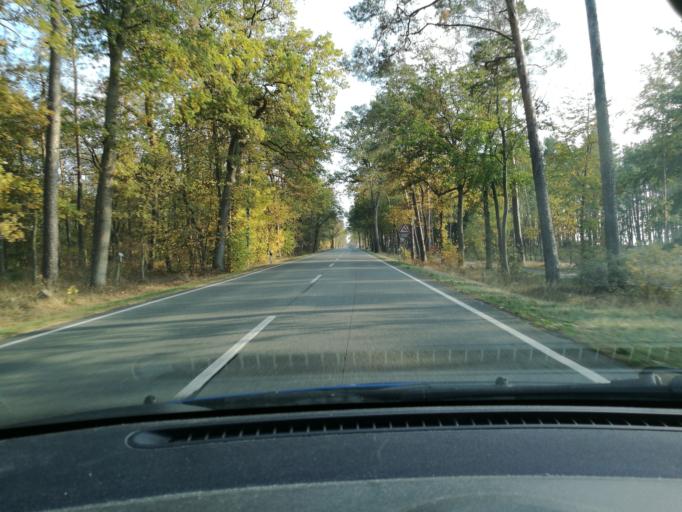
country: DE
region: Lower Saxony
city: Kusten
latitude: 52.9991
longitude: 11.1072
